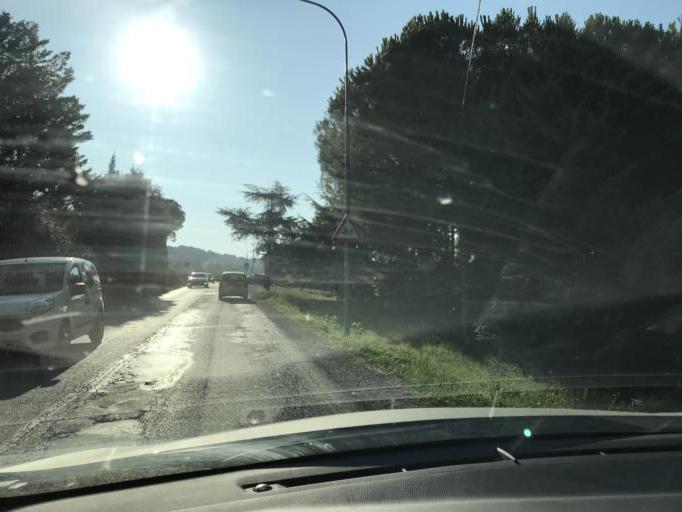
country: IT
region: Umbria
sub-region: Provincia di Perugia
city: Lacugnano
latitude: 43.1142
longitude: 12.3565
